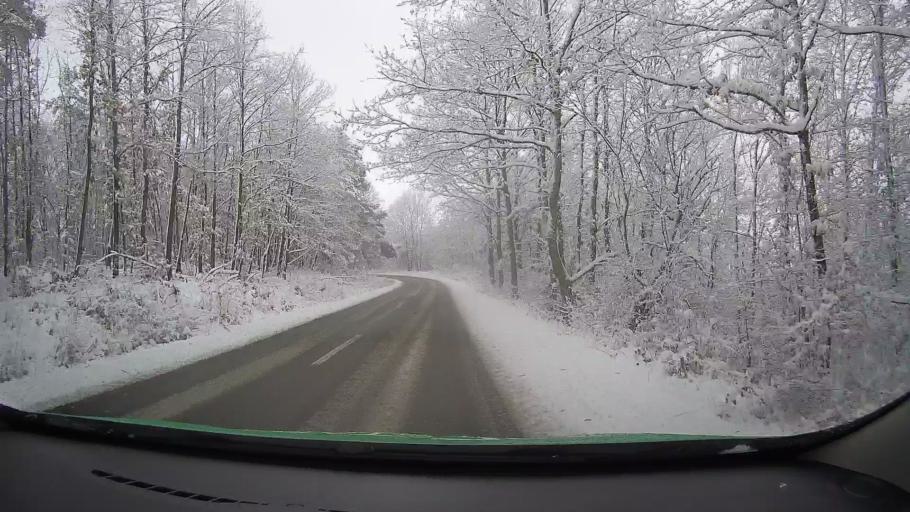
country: RO
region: Hunedoara
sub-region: Comuna Teliucu Inferior
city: Teliucu Inferior
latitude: 45.6733
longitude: 22.9150
